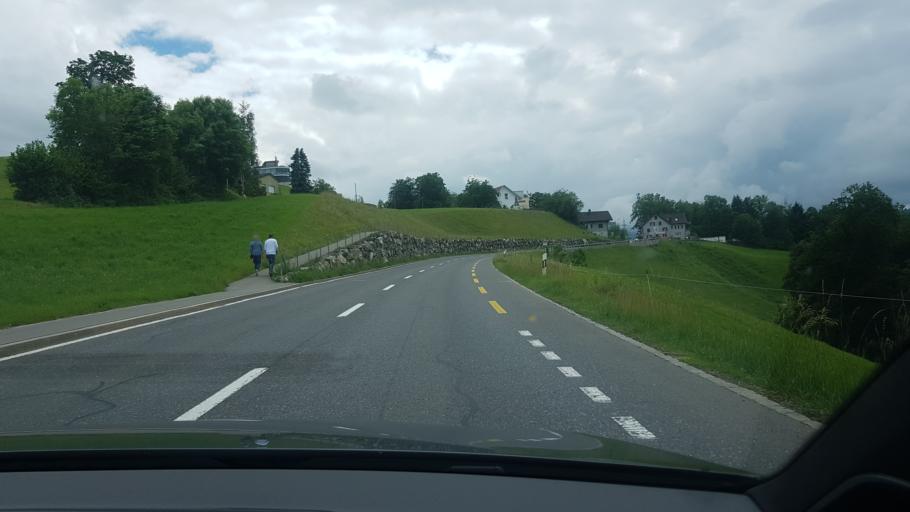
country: CH
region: Zug
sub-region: Zug
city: Menzingen
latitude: 47.1854
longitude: 8.5702
